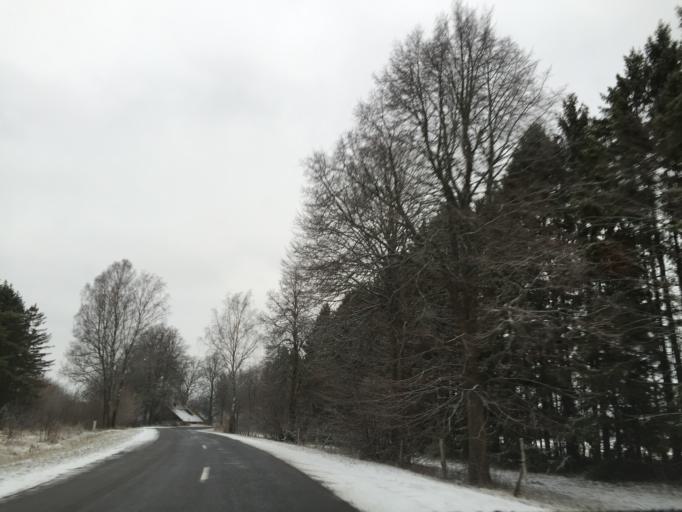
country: EE
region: Saare
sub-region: Orissaare vald
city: Orissaare
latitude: 58.6086
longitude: 23.3070
